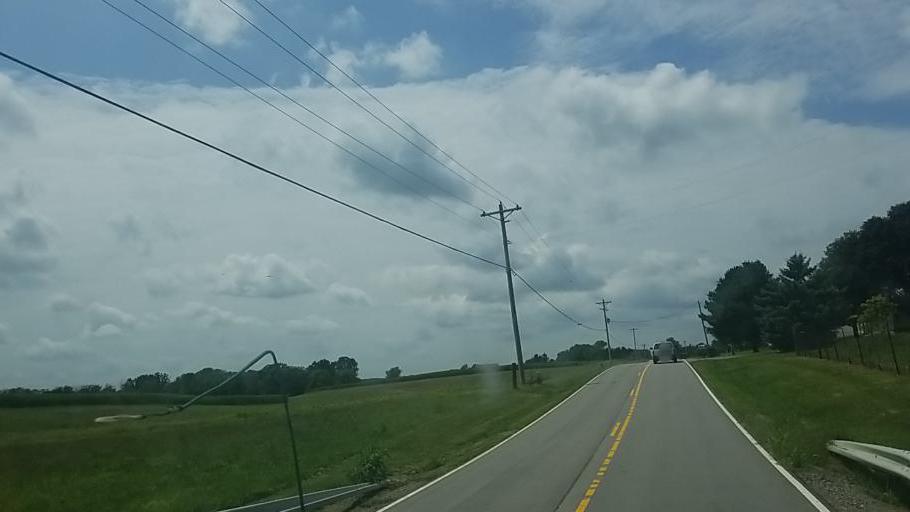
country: US
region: Ohio
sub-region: Fairfield County
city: Lithopolis
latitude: 39.7483
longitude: -82.7764
